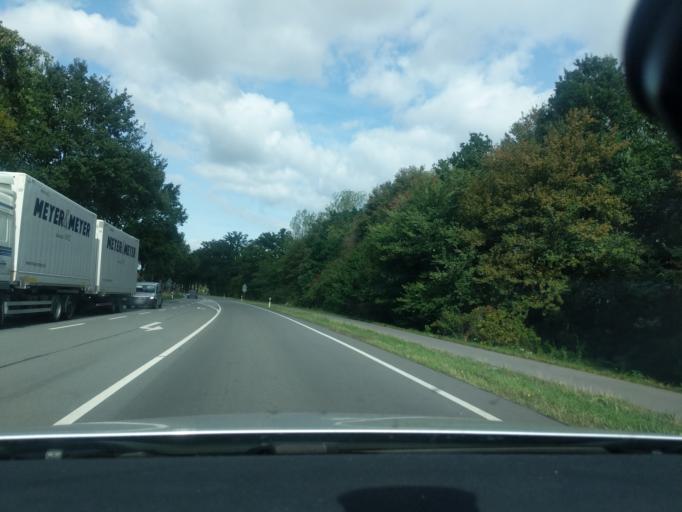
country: DE
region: Lower Saxony
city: Bohmte
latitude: 52.3810
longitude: 8.3109
